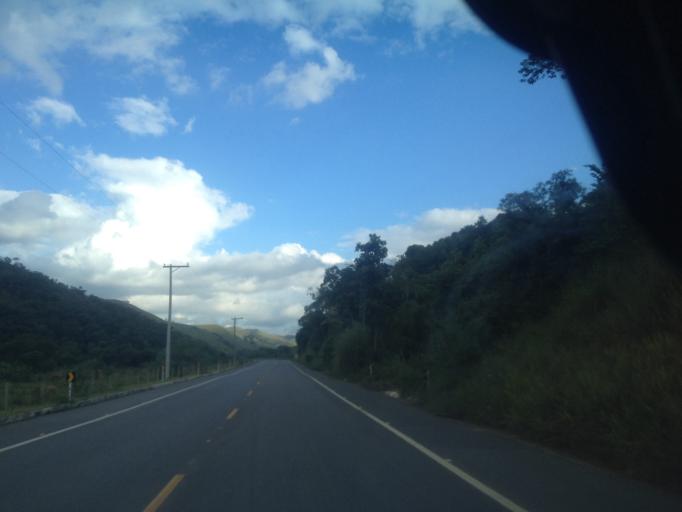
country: BR
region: Rio de Janeiro
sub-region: Quatis
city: Quatis
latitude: -22.2592
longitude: -44.2623
